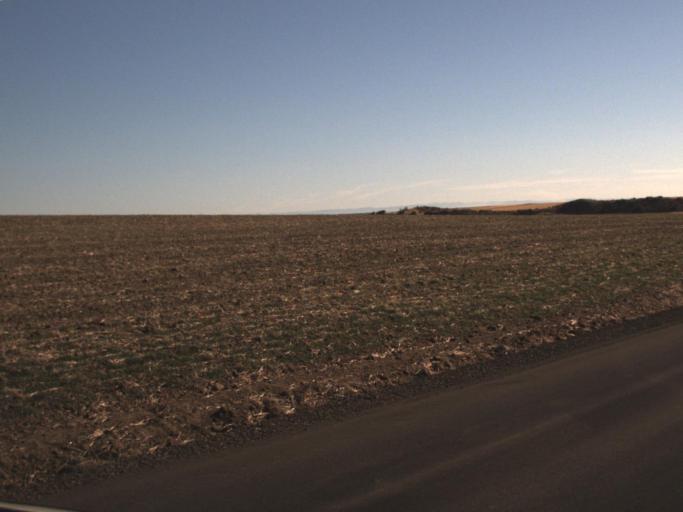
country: US
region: Washington
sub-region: Franklin County
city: Connell
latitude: 46.7893
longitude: -118.5473
